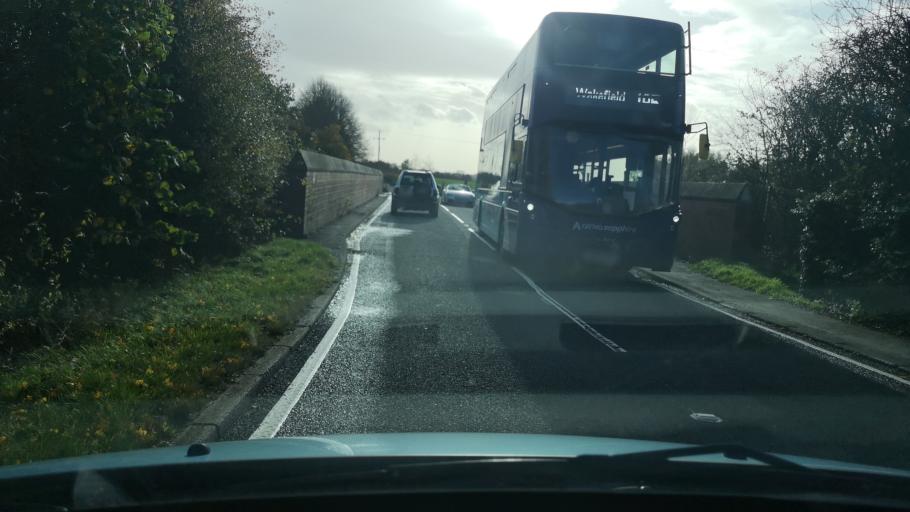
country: GB
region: England
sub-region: City and Borough of Wakefield
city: Crofton
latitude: 53.6491
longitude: -1.4188
